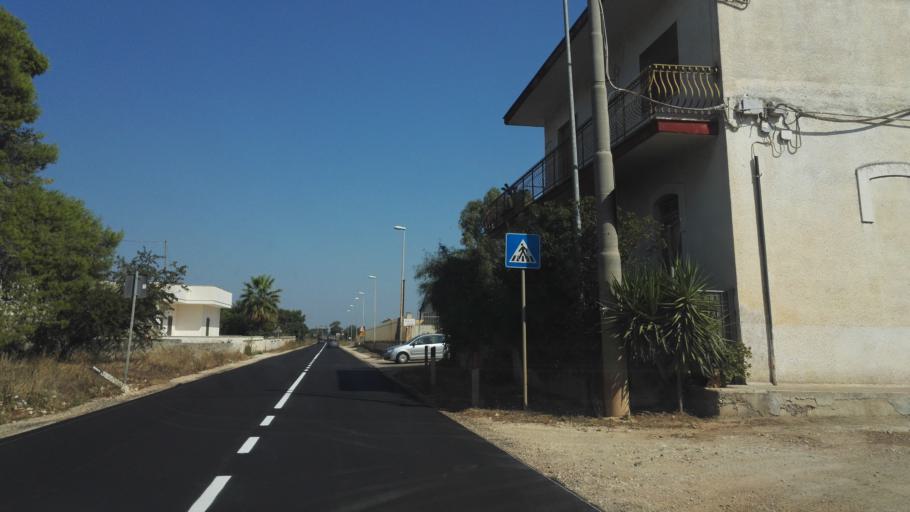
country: IT
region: Apulia
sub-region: Provincia di Lecce
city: Nardo
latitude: 40.2023
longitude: 17.9575
